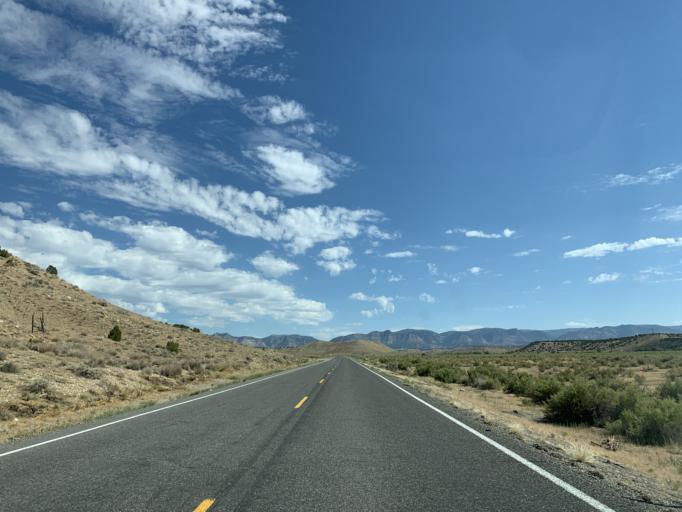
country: US
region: Utah
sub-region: Carbon County
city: Wellington
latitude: 39.5744
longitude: -110.6533
